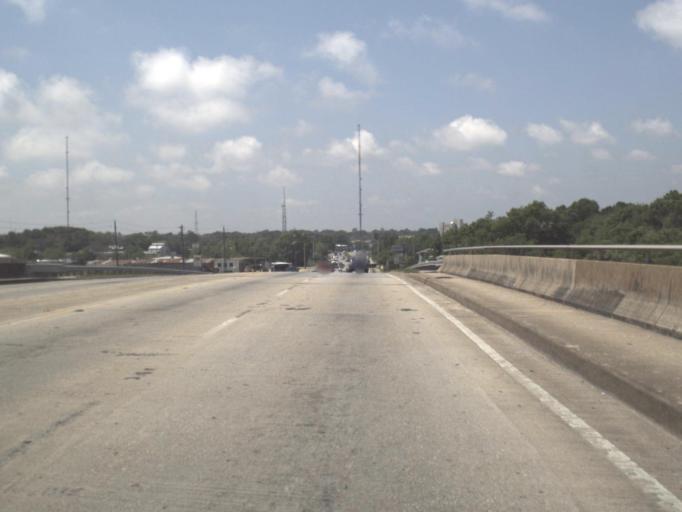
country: US
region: Florida
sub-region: Escambia County
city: Goulding
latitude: 30.4492
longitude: -87.2261
